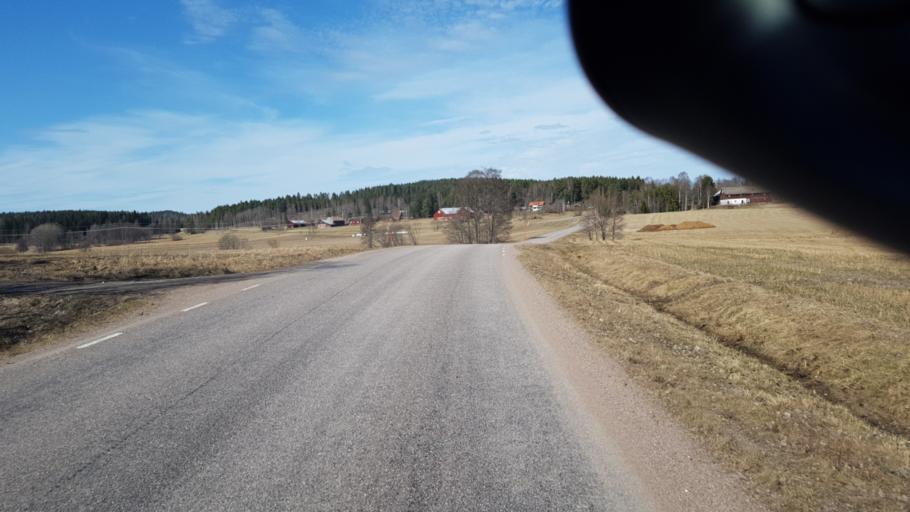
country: SE
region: Vaermland
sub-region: Arvika Kommun
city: Arvika
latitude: 59.6322
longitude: 12.7973
